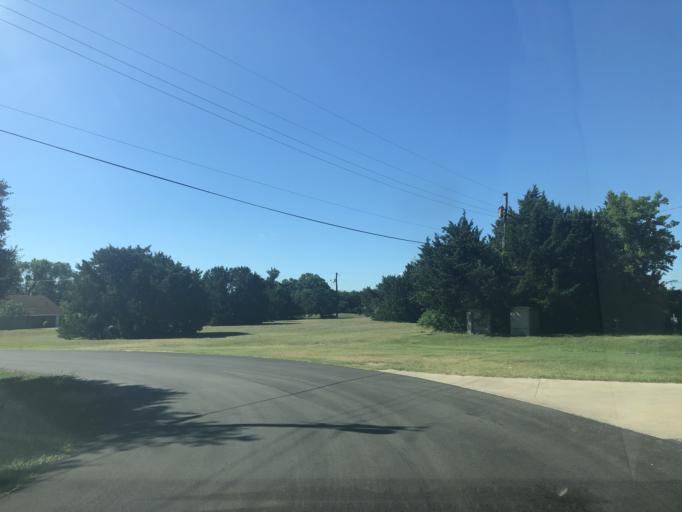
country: US
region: Texas
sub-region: Dallas County
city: Duncanville
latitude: 32.6485
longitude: -96.9408
